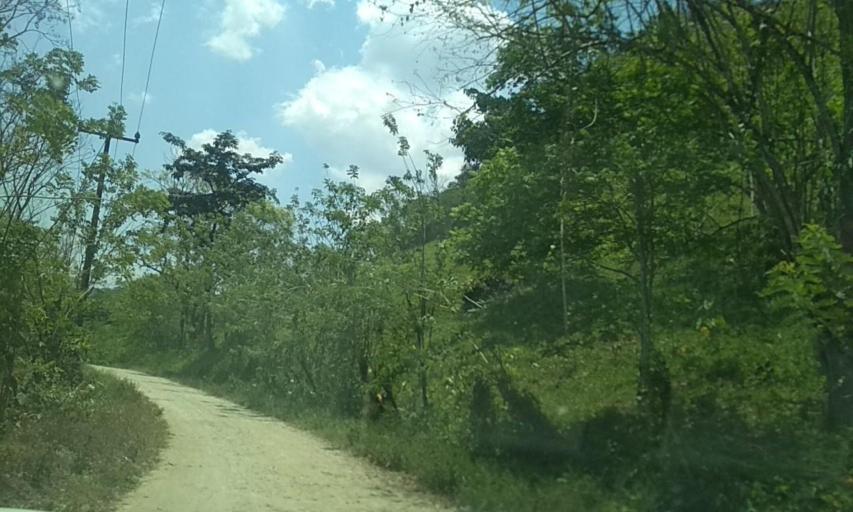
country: MX
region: Chiapas
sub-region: Tecpatan
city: Raudales Malpaso
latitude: 17.2817
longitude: -93.8226
